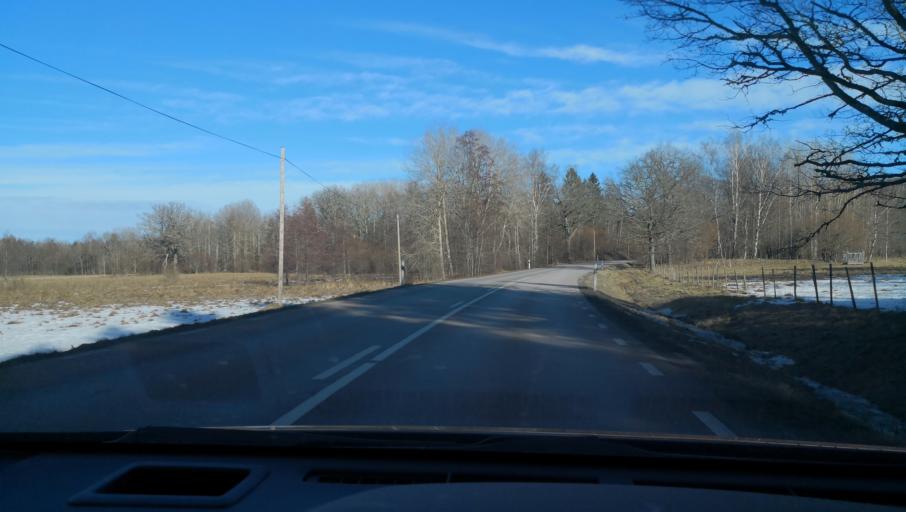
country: SE
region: Uppsala
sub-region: Osthammars Kommun
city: Osterbybruk
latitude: 60.1855
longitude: 17.8644
